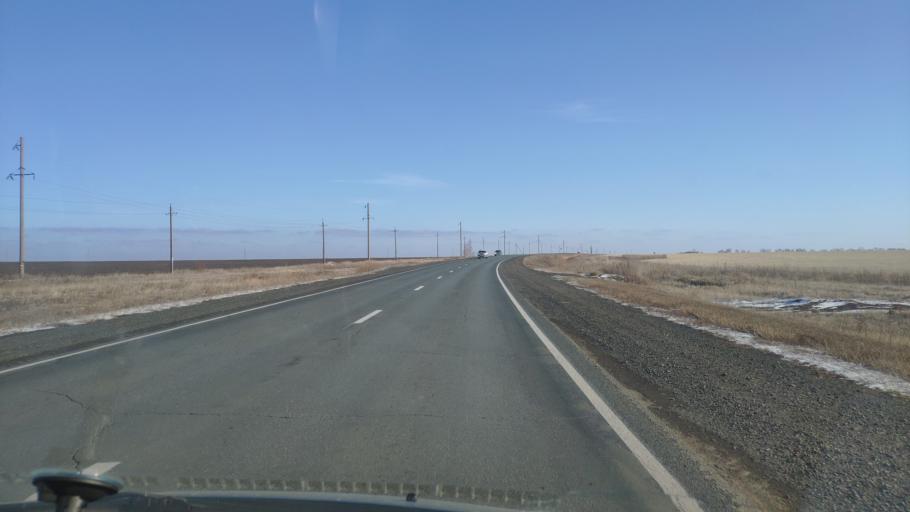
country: RU
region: Orenburg
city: Novorudnyy
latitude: 51.4353
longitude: 57.8964
